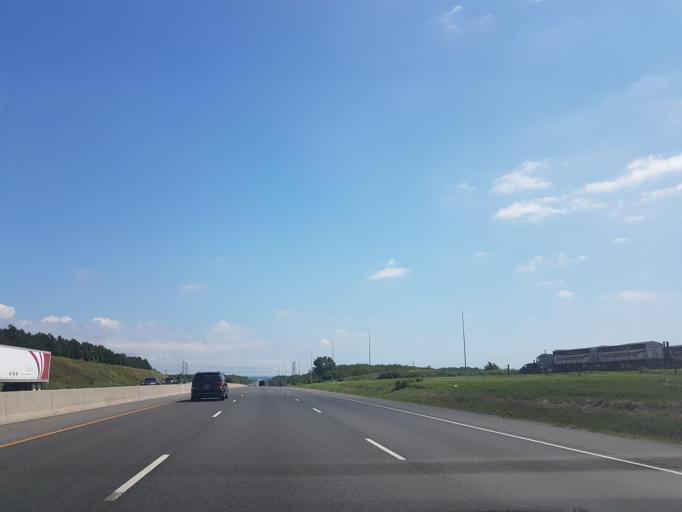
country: CA
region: Ontario
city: Cobourg
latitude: 43.9440
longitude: -78.4308
